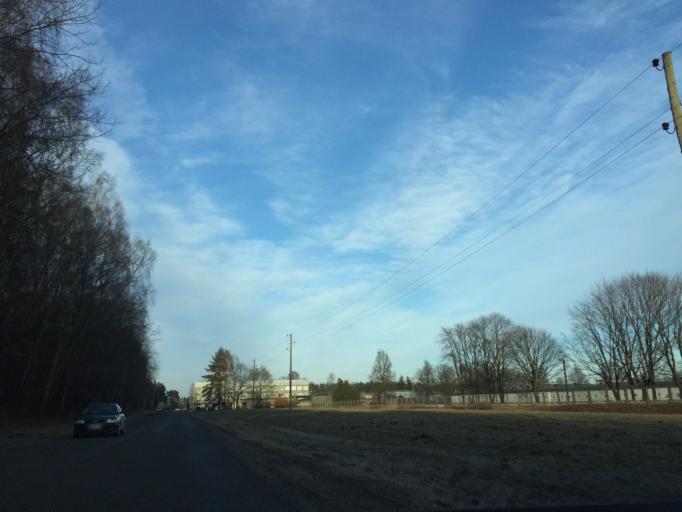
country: LV
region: Kekava
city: Kekava
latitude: 56.8272
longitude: 24.1942
